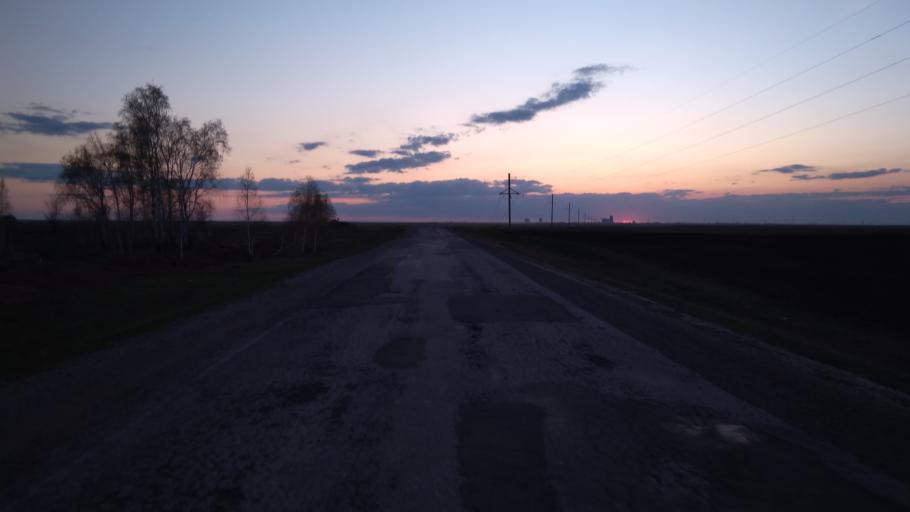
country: RU
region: Chelyabinsk
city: Troitsk
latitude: 54.0863
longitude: 61.6651
